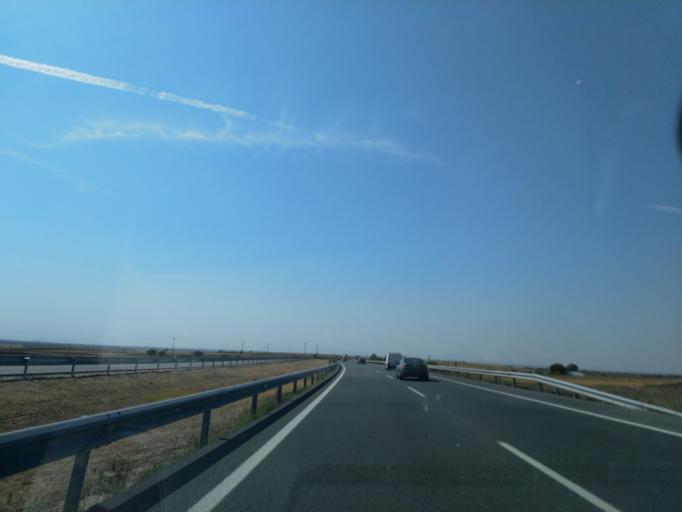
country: ES
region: Castille-La Mancha
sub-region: Province of Toledo
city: Quismondo
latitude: 40.1057
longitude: -4.3334
